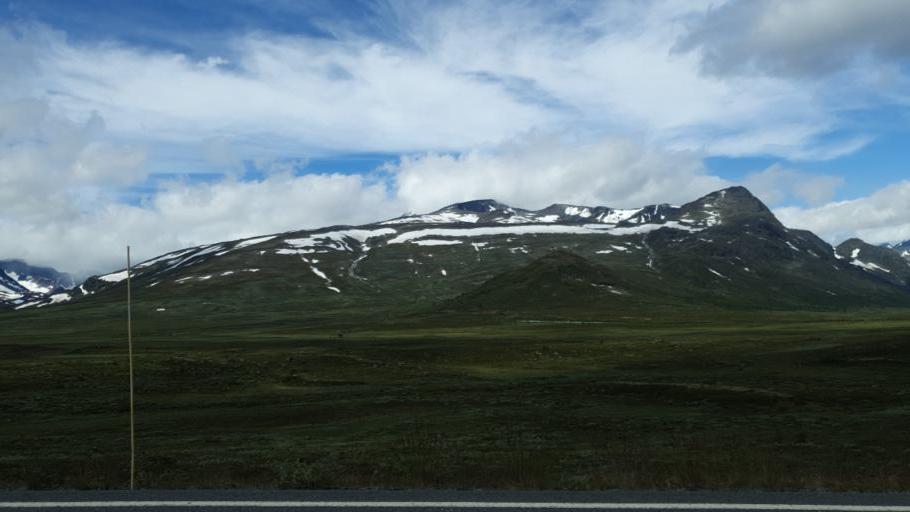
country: NO
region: Oppland
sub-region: Vang
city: Vang
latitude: 61.4532
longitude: 8.8060
